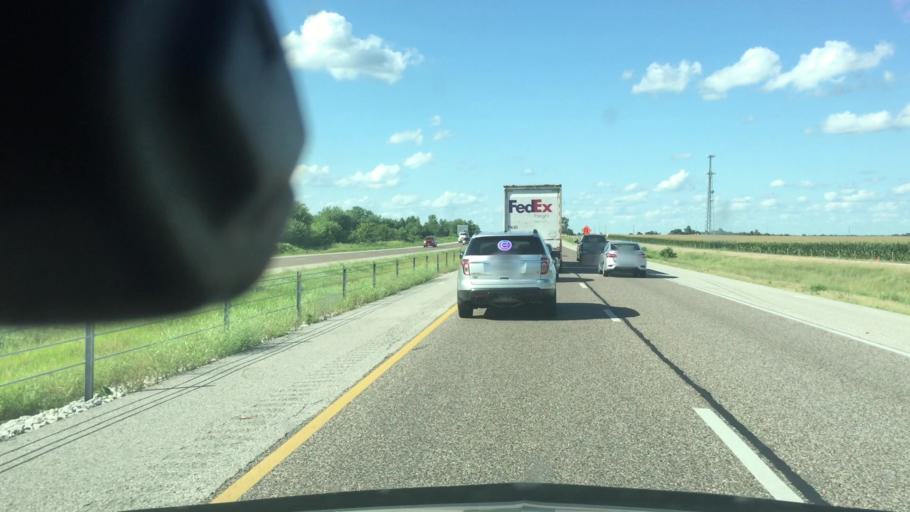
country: US
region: Illinois
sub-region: Madison County
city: Edwardsville
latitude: 38.8089
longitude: -89.8915
